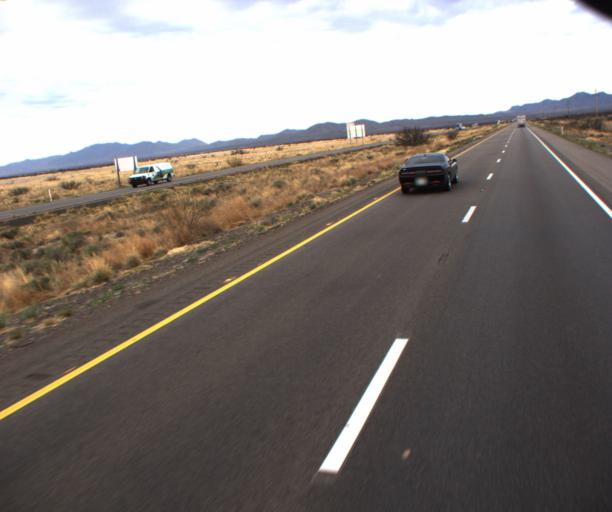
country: US
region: Arizona
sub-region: Cochise County
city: Willcox
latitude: 32.2081
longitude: -109.8966
